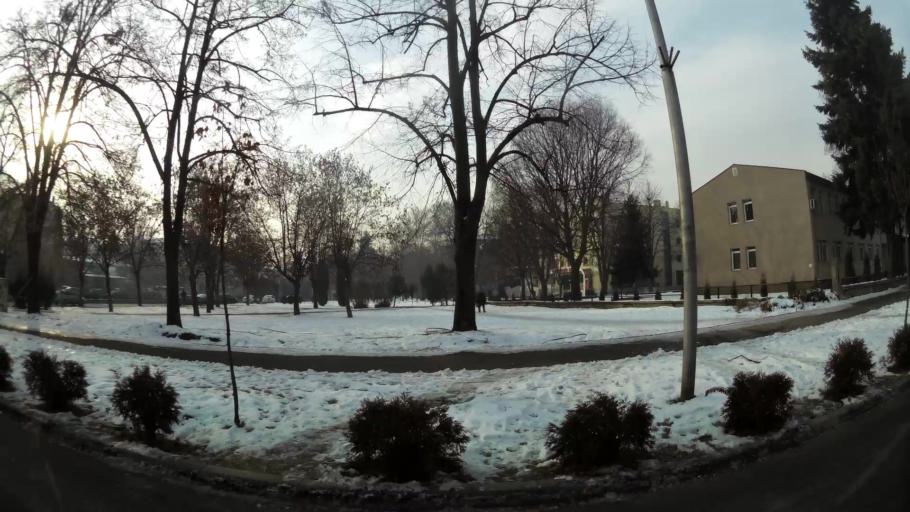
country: MK
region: Cair
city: Cair
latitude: 42.0213
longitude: 21.4486
